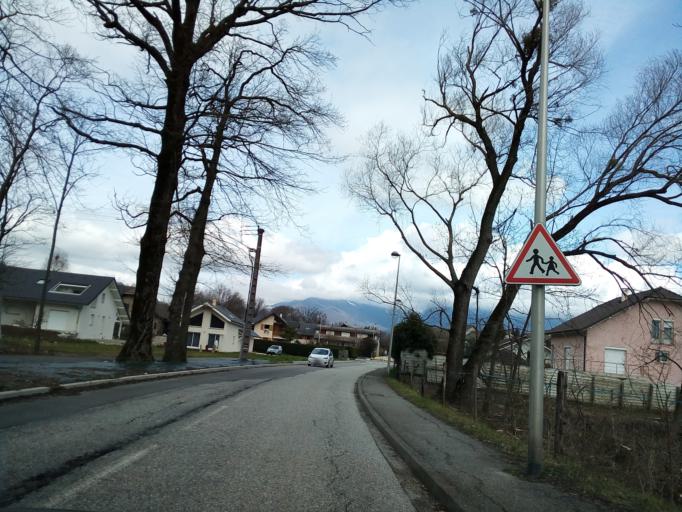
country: FR
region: Rhone-Alpes
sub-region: Departement de la Savoie
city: Saint-Baldoph
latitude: 45.5286
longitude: 5.9552
